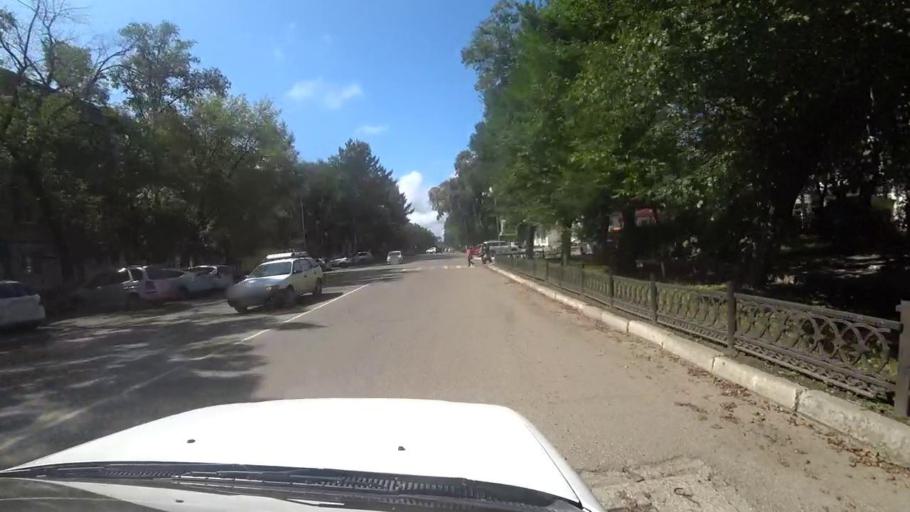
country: RU
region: Primorskiy
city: Dal'nerechensk
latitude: 45.9327
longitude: 133.7319
